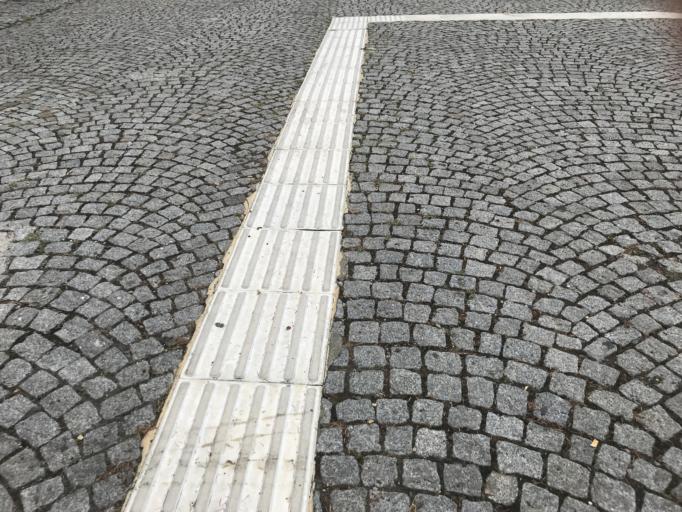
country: TR
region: Ankara
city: Ankara
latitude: 39.9165
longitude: 32.8275
